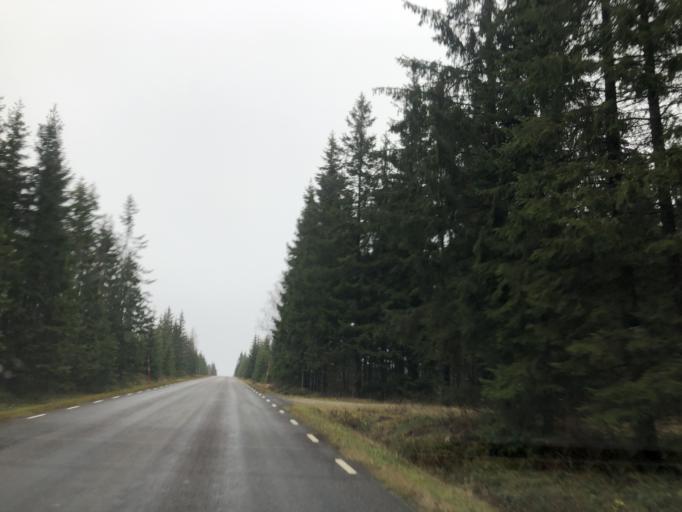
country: SE
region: Vaestra Goetaland
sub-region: Ulricehamns Kommun
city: Ulricehamn
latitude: 57.7339
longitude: 13.5433
